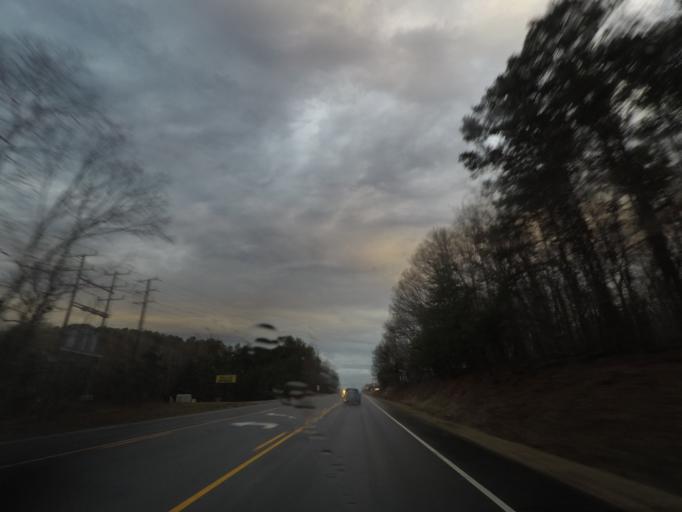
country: US
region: North Carolina
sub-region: Caswell County
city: Yanceyville
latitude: 36.4122
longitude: -79.3439
